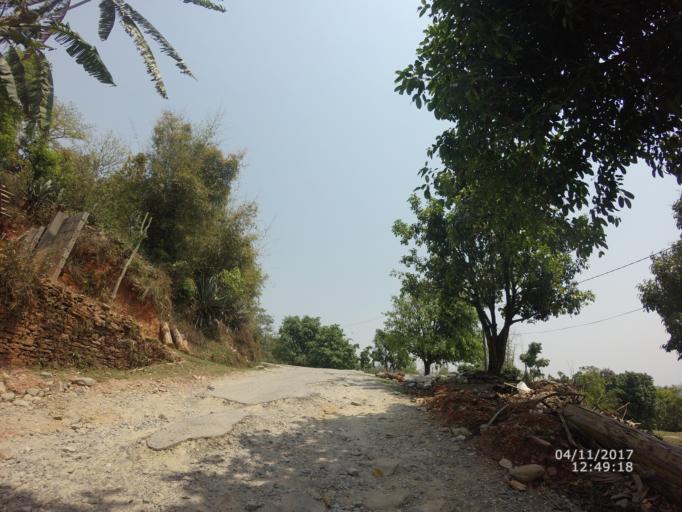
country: NP
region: Western Region
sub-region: Gandaki Zone
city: Pokhara
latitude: 28.2073
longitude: 84.0353
